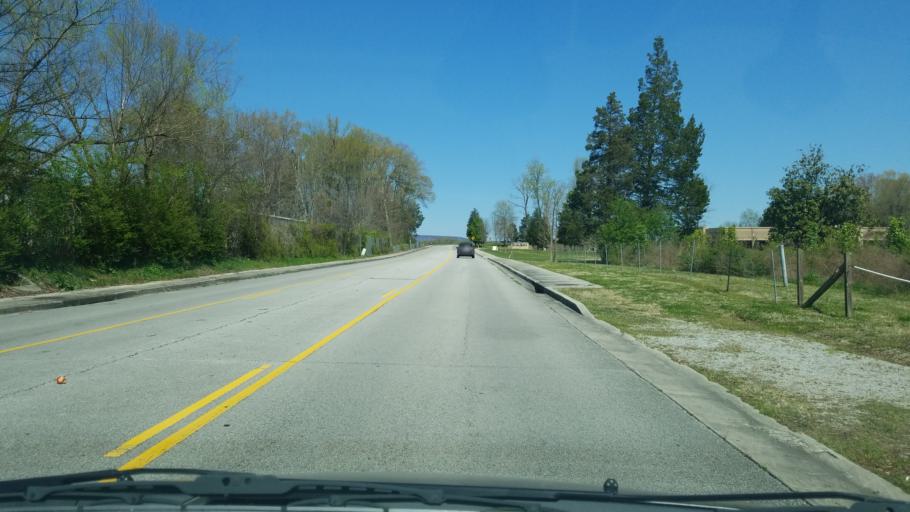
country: US
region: Tennessee
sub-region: Hamilton County
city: Red Bank
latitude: 35.1253
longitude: -85.2357
